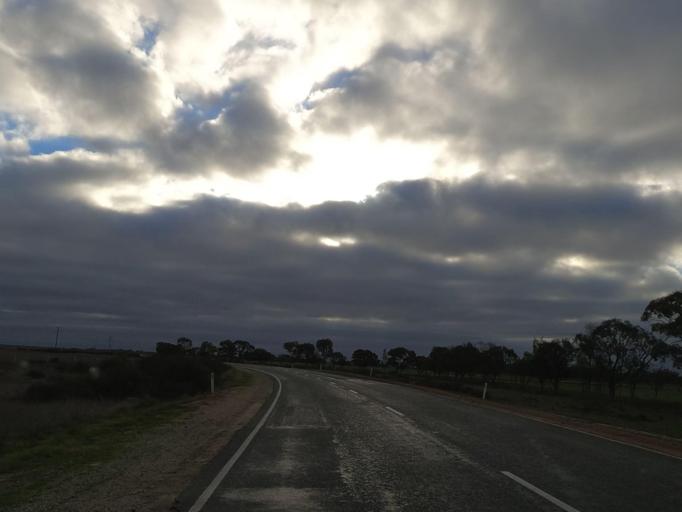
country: AU
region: Victoria
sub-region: Swan Hill
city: Swan Hill
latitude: -35.6514
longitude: 143.8445
